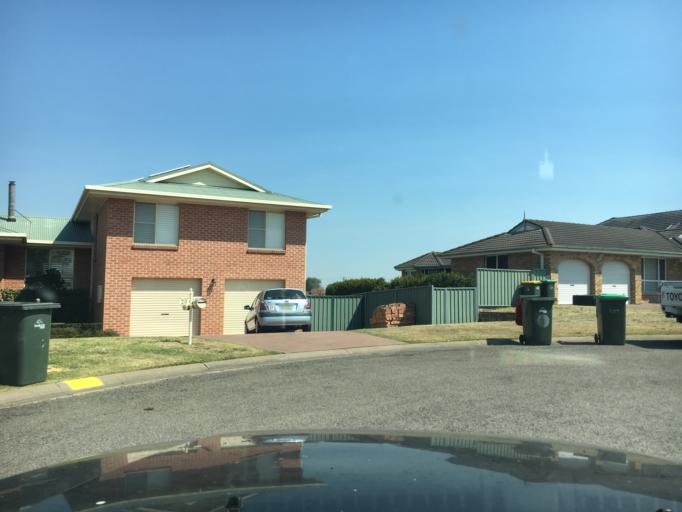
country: AU
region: New South Wales
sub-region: Singleton
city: Singleton
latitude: -32.5747
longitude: 151.1869
